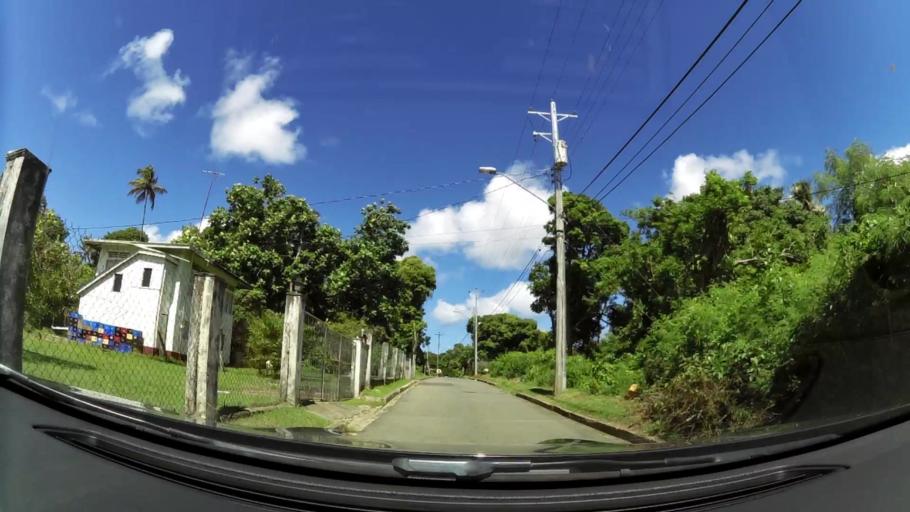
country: TT
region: Tobago
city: Scarborough
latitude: 11.1688
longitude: -60.7835
